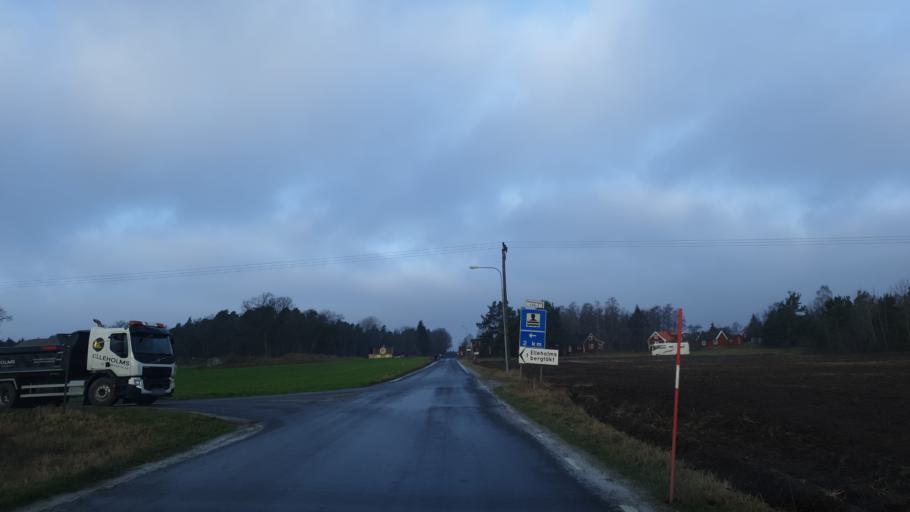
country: SE
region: Blekinge
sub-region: Karlshamns Kommun
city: Morrum
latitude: 56.1695
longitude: 14.7434
